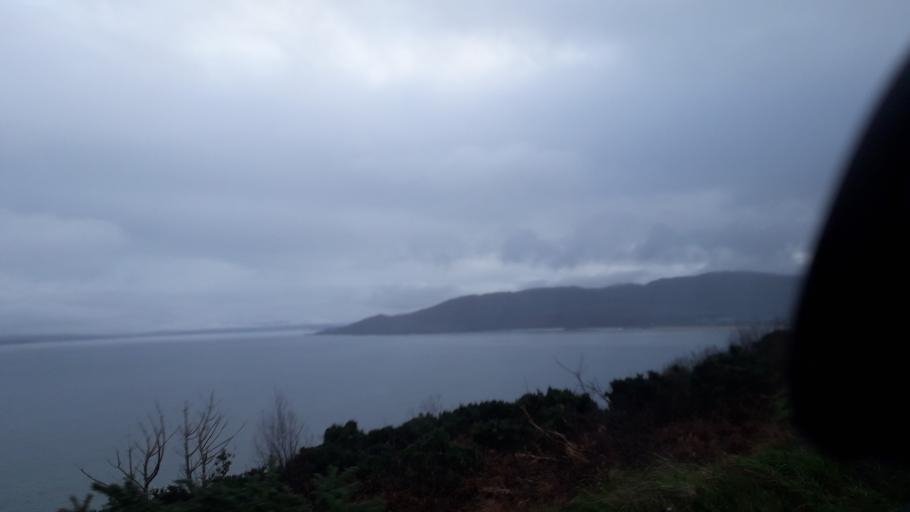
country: IE
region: Ulster
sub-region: County Donegal
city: Ramelton
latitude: 55.2140
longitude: -7.6139
